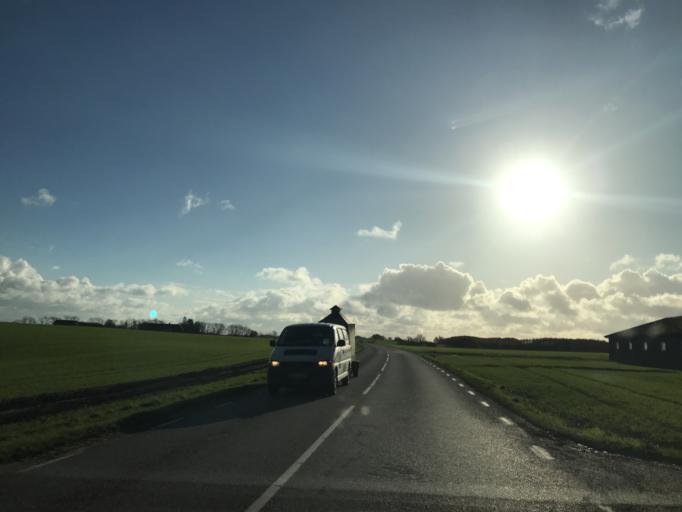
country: SE
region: Skane
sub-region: Skurups Kommun
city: Skurup
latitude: 55.4552
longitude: 13.4769
